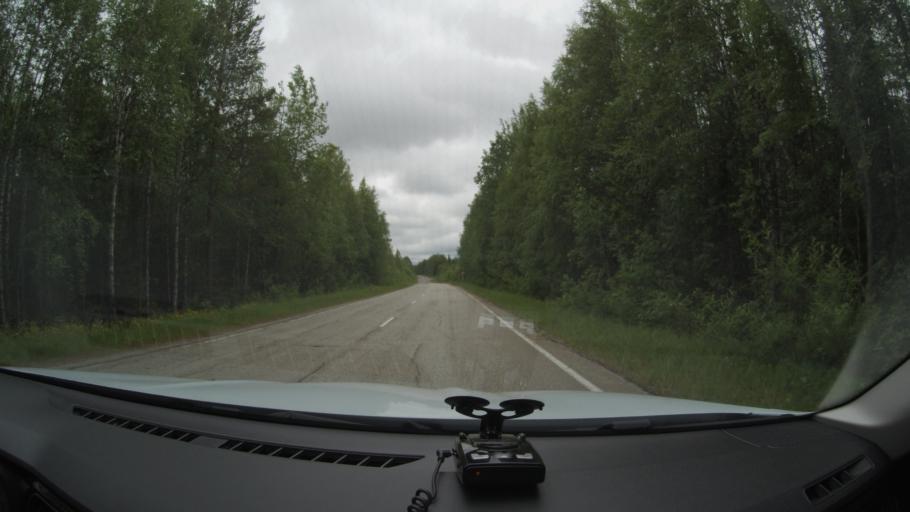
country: RU
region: Komi Republic
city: Nizhniy Odes
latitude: 63.6206
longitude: 54.6063
